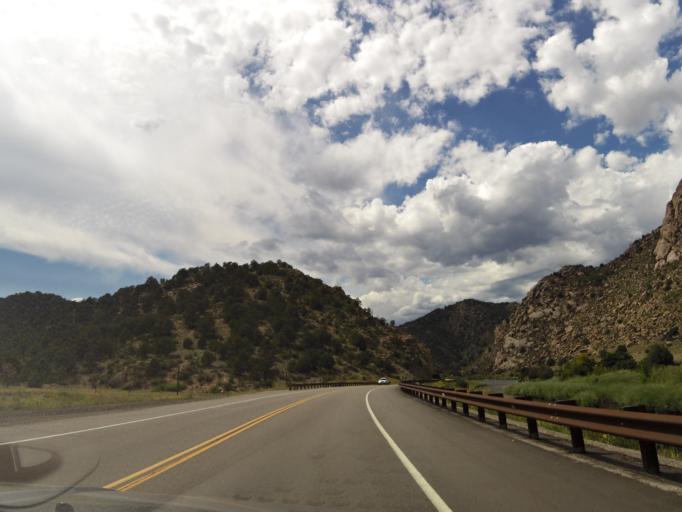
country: US
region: Colorado
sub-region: Custer County
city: Westcliffe
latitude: 38.3903
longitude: -105.6444
